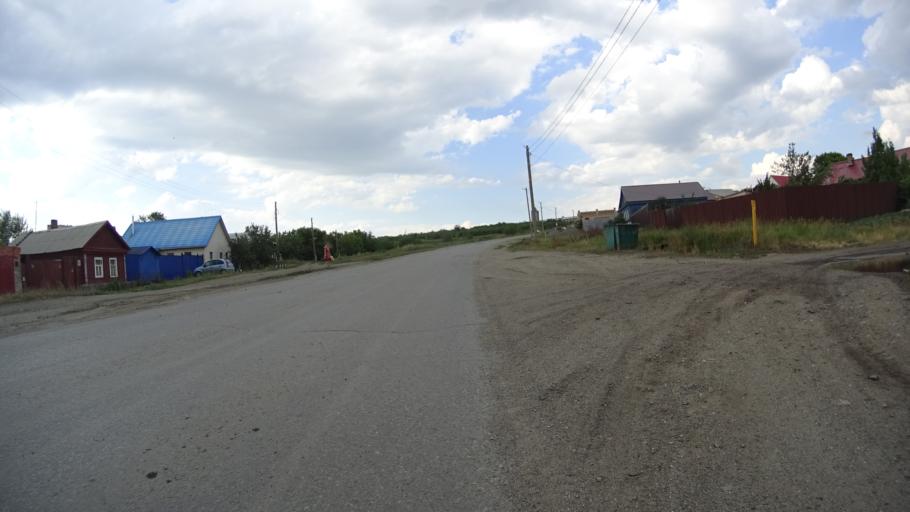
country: RU
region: Chelyabinsk
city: Troitsk
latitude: 54.0996
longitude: 61.5912
